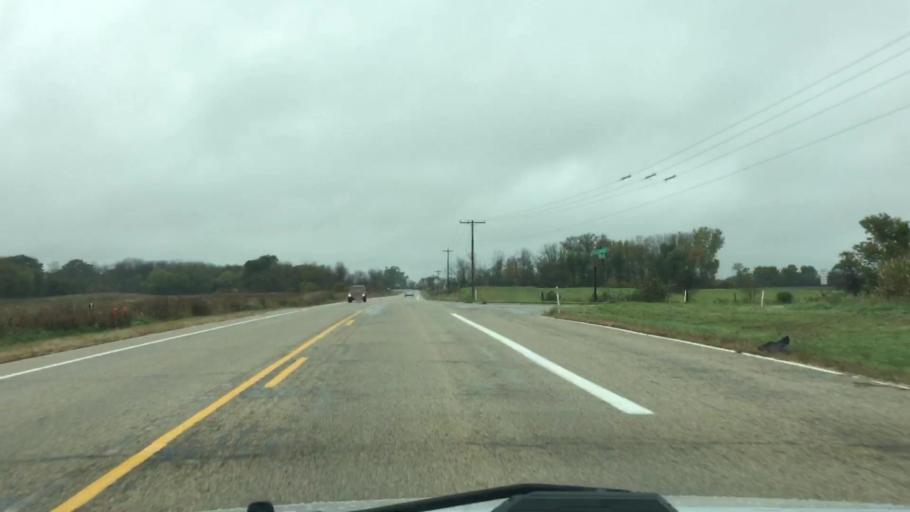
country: US
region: Wisconsin
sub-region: Jefferson County
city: Palmyra
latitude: 42.8795
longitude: -88.6151
